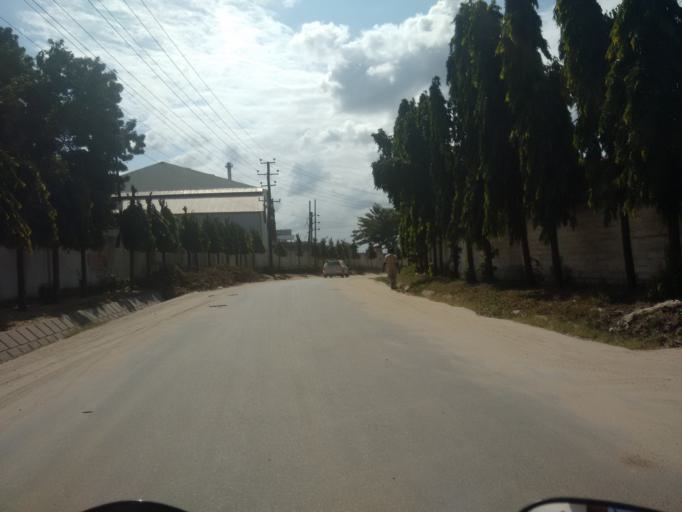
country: TZ
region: Dar es Salaam
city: Dar es Salaam
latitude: -6.8450
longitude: 39.2544
